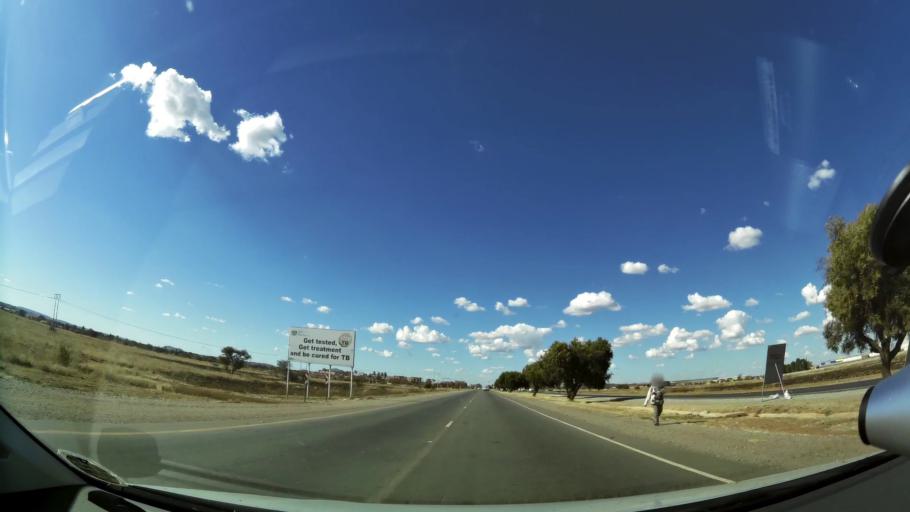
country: ZA
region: North-West
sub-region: Dr Kenneth Kaunda District Municipality
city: Klerksdorp
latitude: -26.8708
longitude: 26.6166
